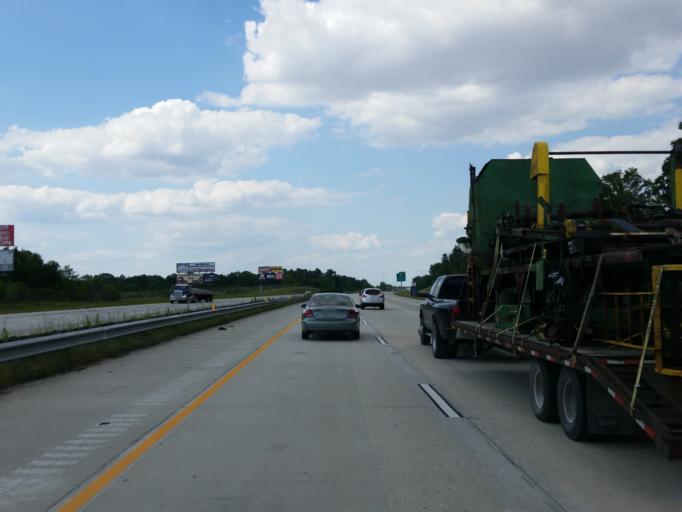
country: US
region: Georgia
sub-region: Dooly County
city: Vienna
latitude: 32.1101
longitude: -83.7628
